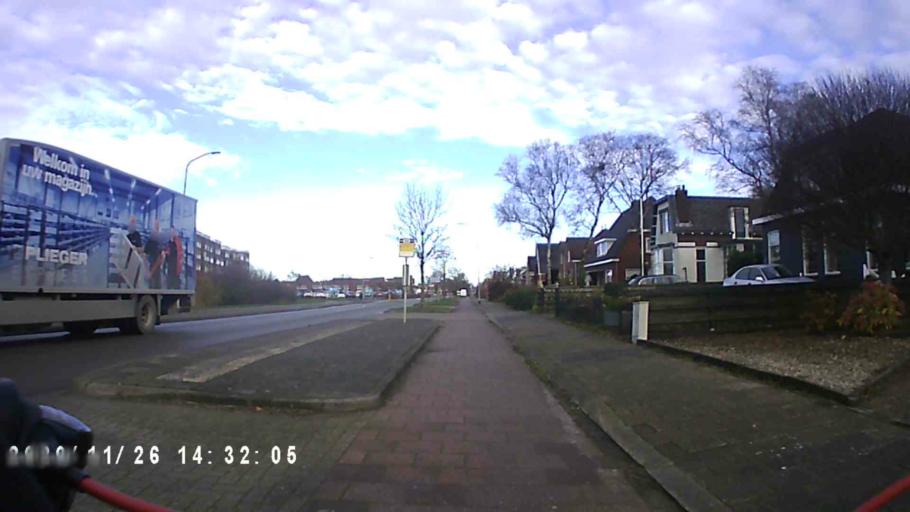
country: NL
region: Groningen
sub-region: Gemeente Appingedam
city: Appingedam
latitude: 53.3170
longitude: 6.8594
